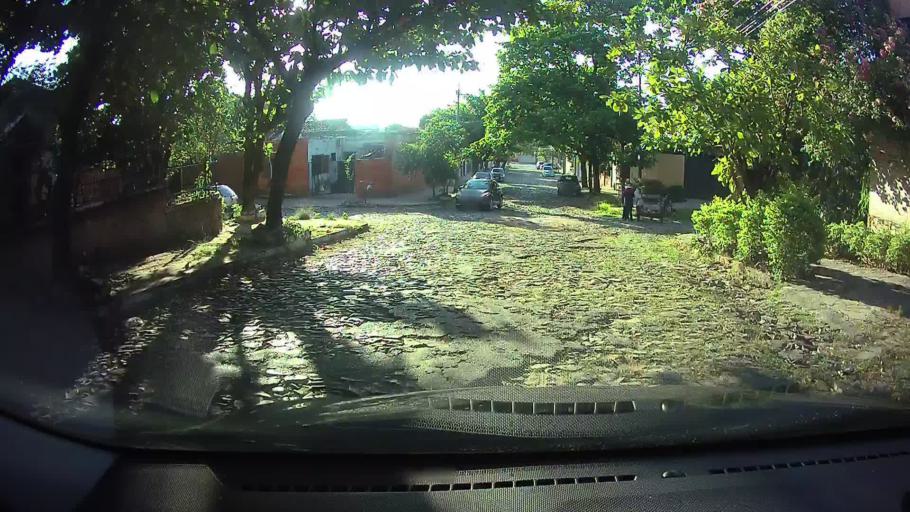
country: PY
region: Asuncion
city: Asuncion
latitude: -25.2717
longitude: -57.5966
